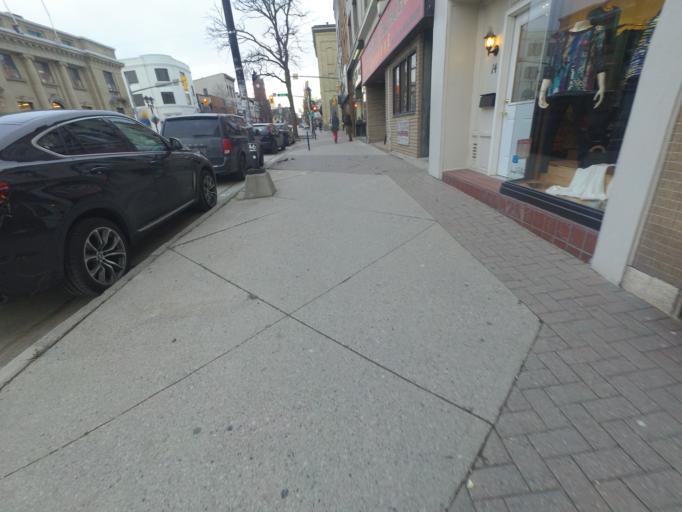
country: CN
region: Xinjiang Uygur Zizhiqu
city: Ayxin Siri
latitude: 43.4646
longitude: 80.5215
